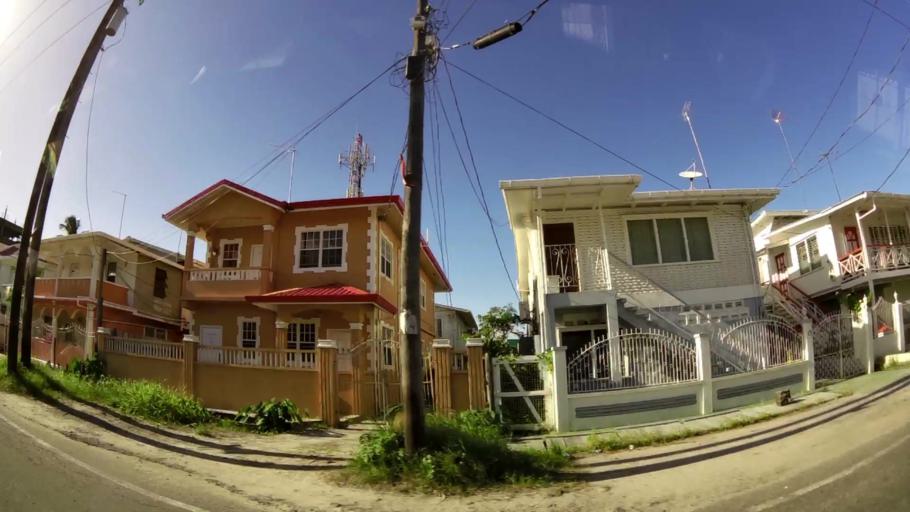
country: GY
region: Demerara-Mahaica
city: Georgetown
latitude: 6.8179
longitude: -58.1437
